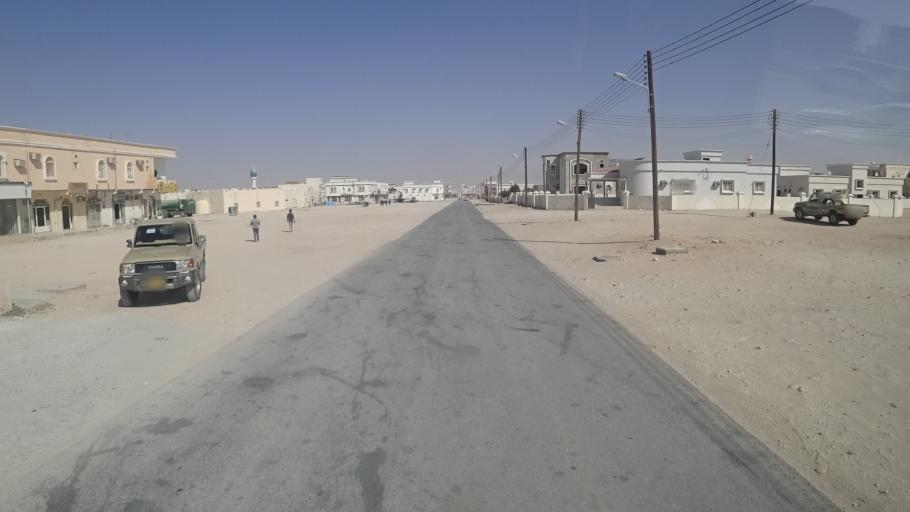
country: YE
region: Al Mahrah
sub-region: Shahan
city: Shihan as Sufla
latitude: 17.8422
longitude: 52.6590
